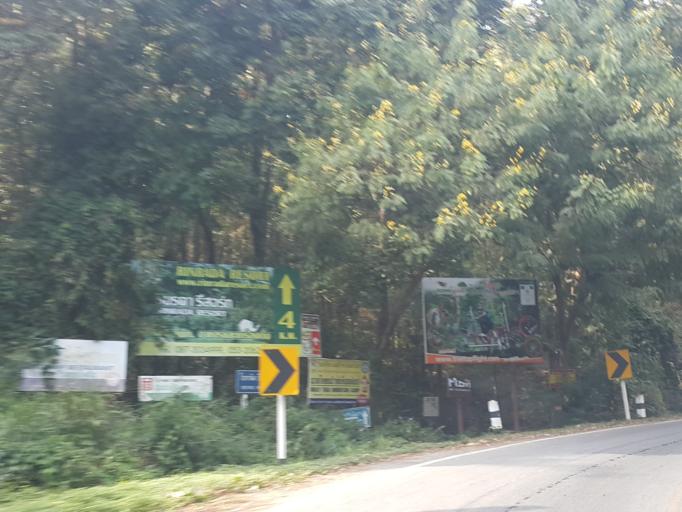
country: TH
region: Chiang Mai
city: Chiang Mai
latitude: 18.9078
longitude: 98.9011
